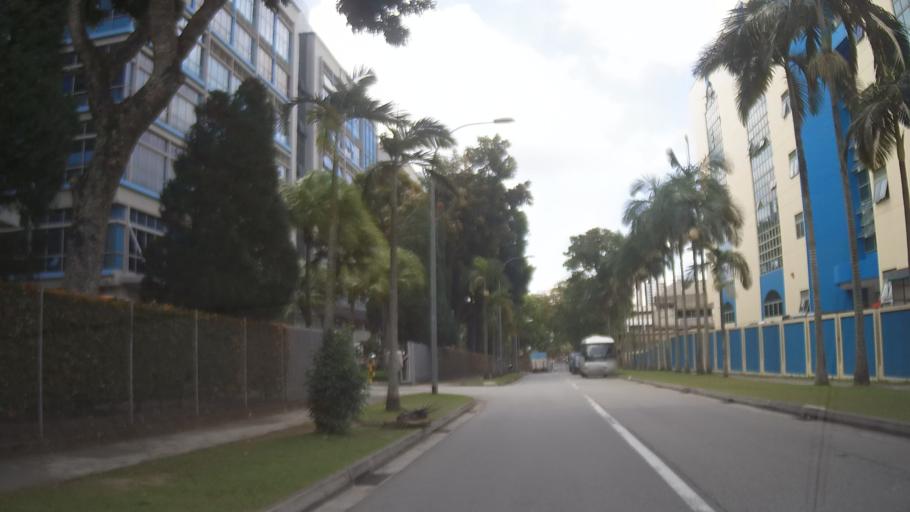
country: MY
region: Johor
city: Johor Bahru
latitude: 1.4061
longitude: 103.7591
